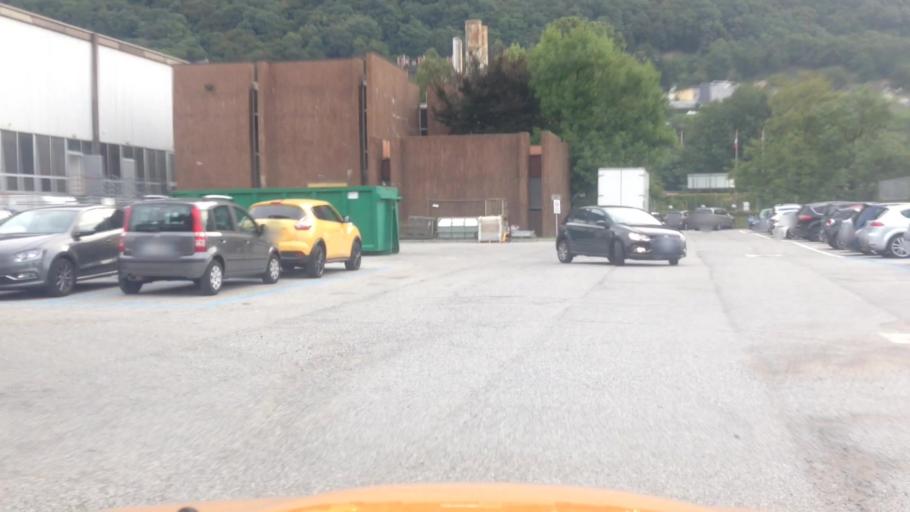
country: CH
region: Ticino
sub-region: Mendrisio District
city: Mendrisio
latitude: 45.8822
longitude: 8.9783
